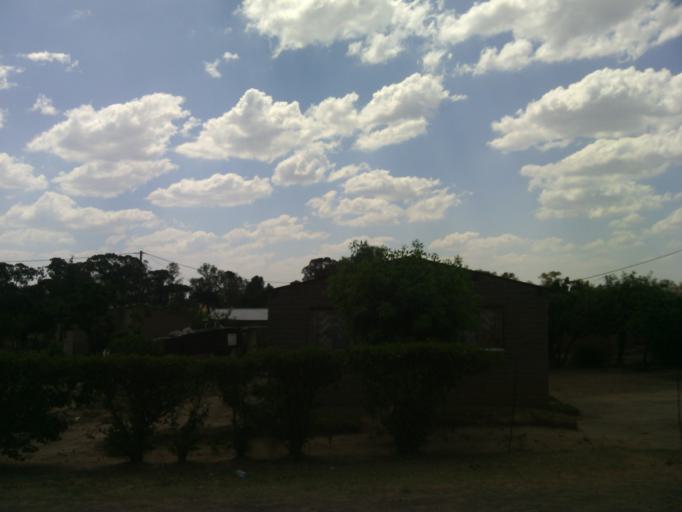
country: ZA
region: Orange Free State
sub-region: Xhariep District Municipality
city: Dewetsdorp
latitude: -29.5780
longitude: 26.6803
